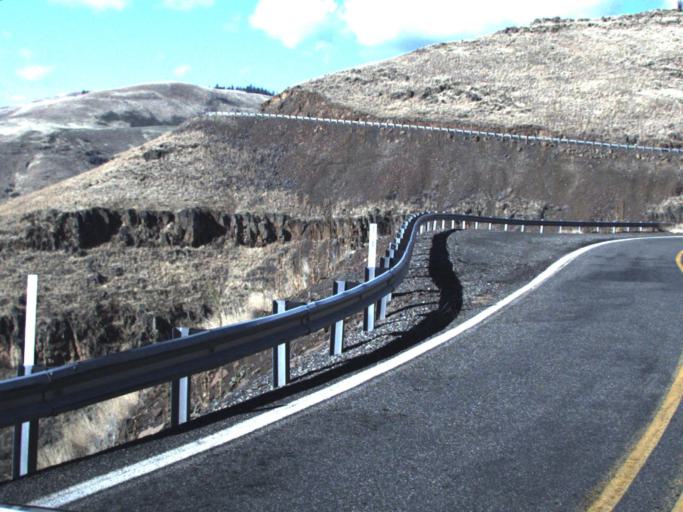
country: US
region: Washington
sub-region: Asotin County
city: Asotin
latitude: 46.0518
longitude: -117.2300
